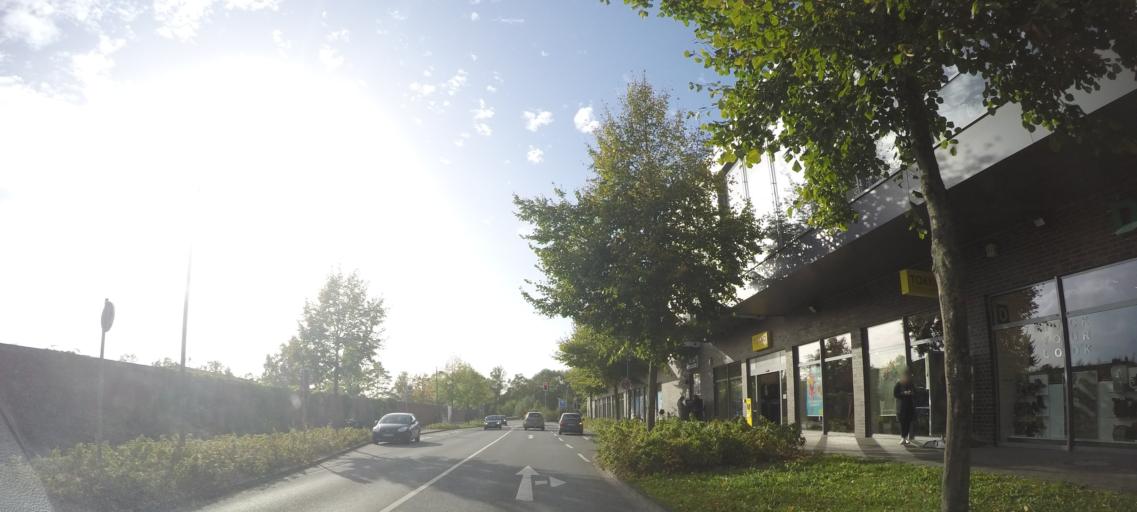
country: DE
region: North Rhine-Westphalia
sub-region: Regierungsbezirk Arnsberg
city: Lippstadt
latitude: 51.6699
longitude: 8.3444
